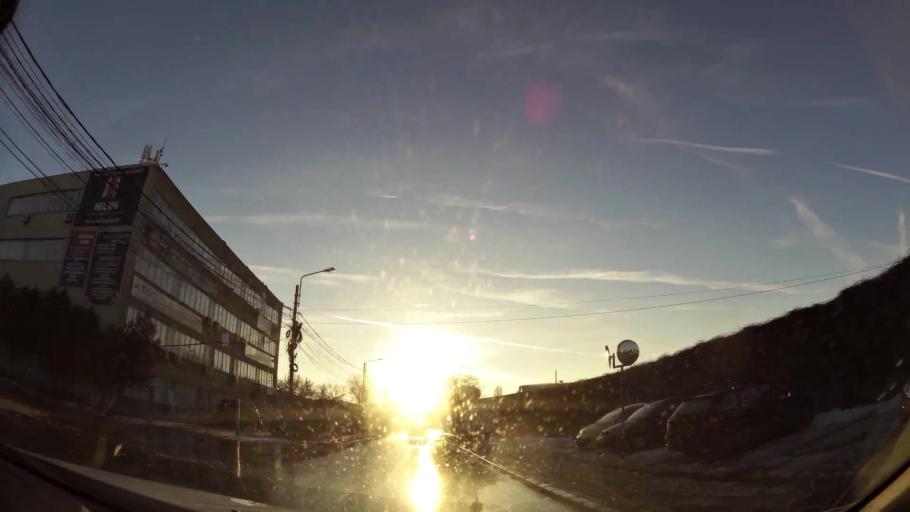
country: RO
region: Ilfov
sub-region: Comuna Fundeni-Dobroesti
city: Fundeni
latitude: 44.4528
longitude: 26.1405
